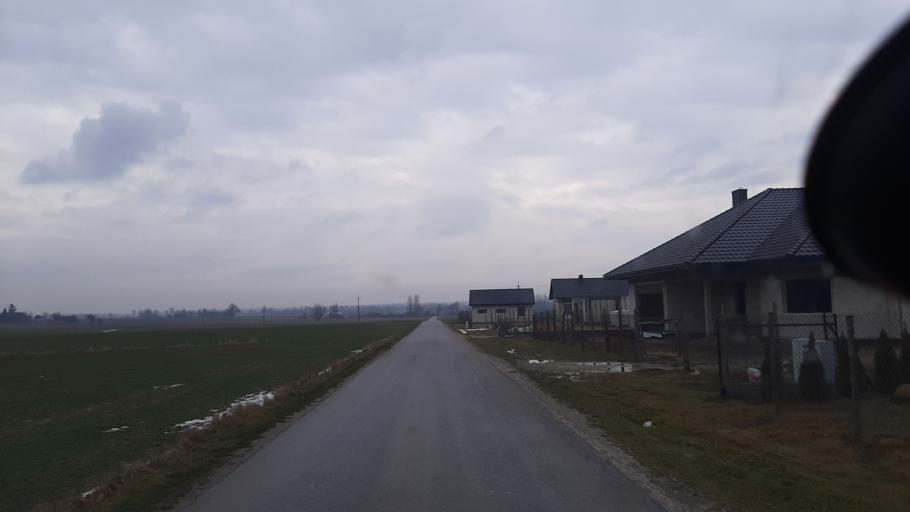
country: PL
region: Lublin Voivodeship
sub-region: Powiat lubelski
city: Jastkow
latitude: 51.3453
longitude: 22.5081
